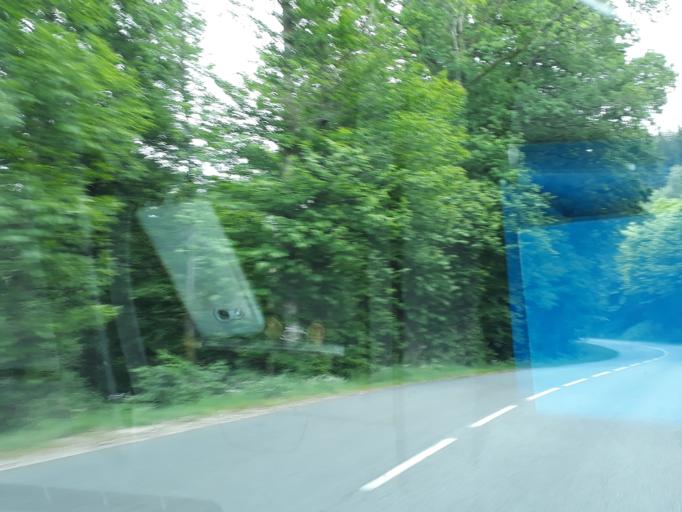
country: FR
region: Limousin
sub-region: Departement de la Haute-Vienne
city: Peyrat-le-Chateau
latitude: 45.8129
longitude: 1.8084
